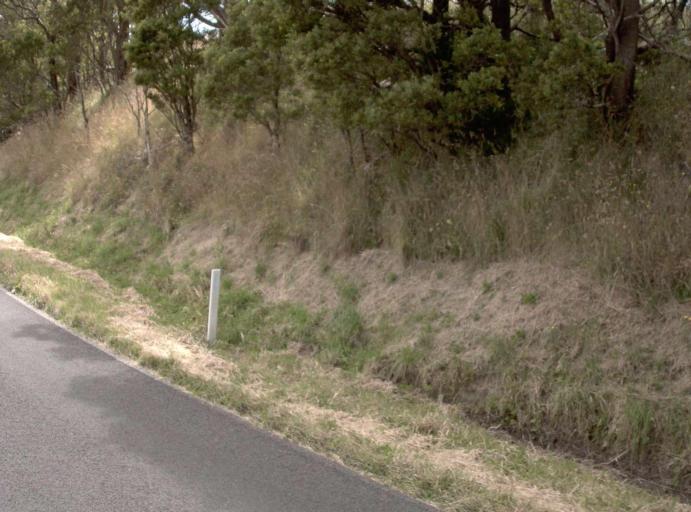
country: AU
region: Victoria
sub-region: Baw Baw
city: Warragul
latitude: -38.3845
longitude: 145.8253
